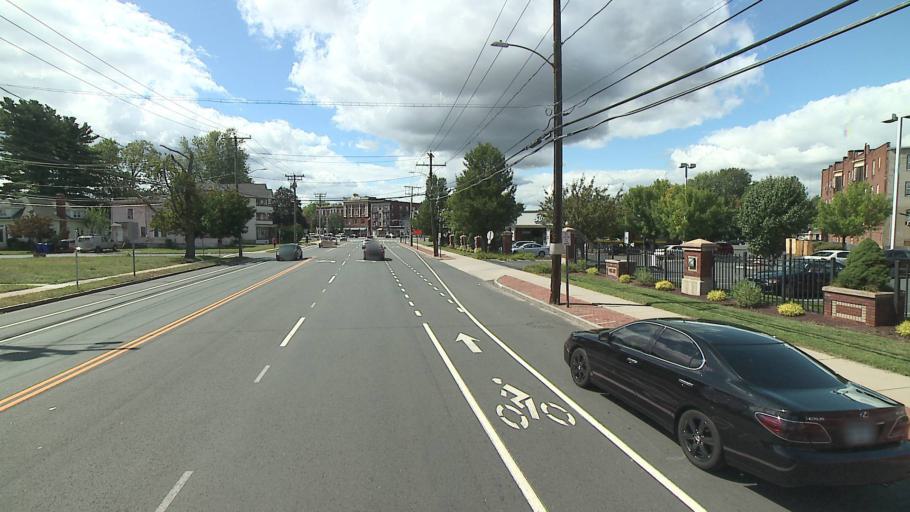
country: US
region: Connecticut
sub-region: Hartford County
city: East Hartford
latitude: 41.7743
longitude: -72.6390
